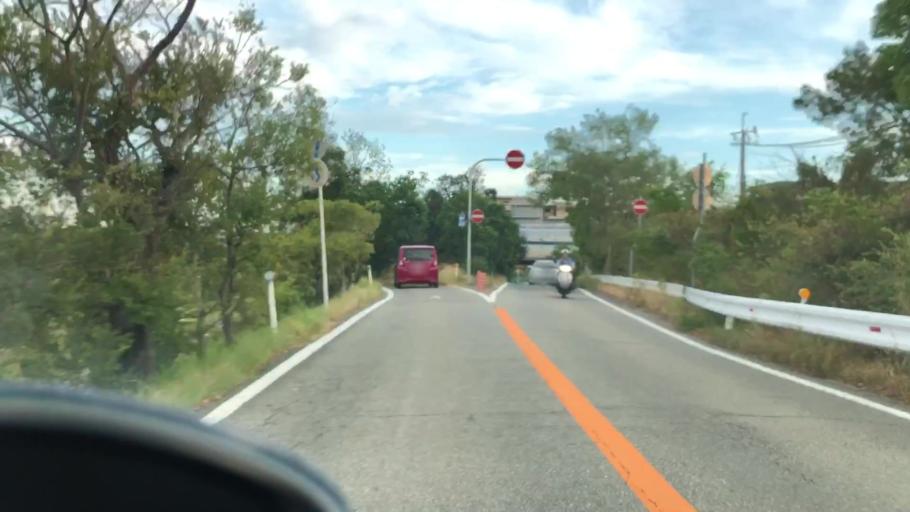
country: JP
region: Hyogo
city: Itami
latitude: 34.7459
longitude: 135.3751
